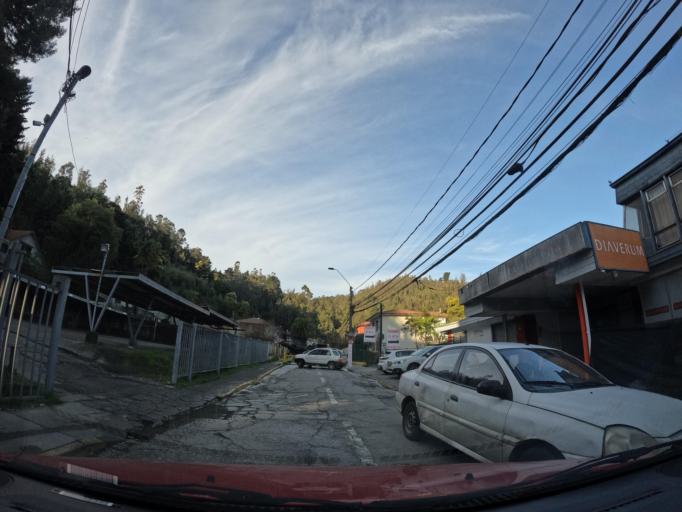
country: CL
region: Biobio
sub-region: Provincia de Concepcion
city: Concepcion
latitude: -36.8437
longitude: -73.0514
